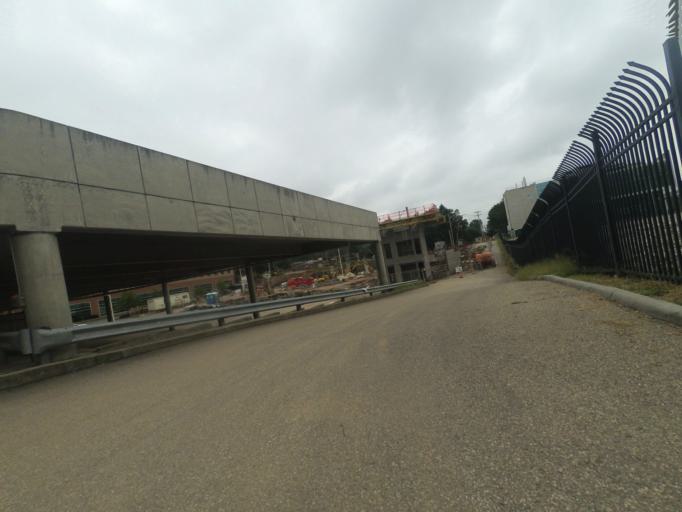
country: US
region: West Virginia
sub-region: Cabell County
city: Huntington
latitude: 38.4117
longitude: -82.4303
